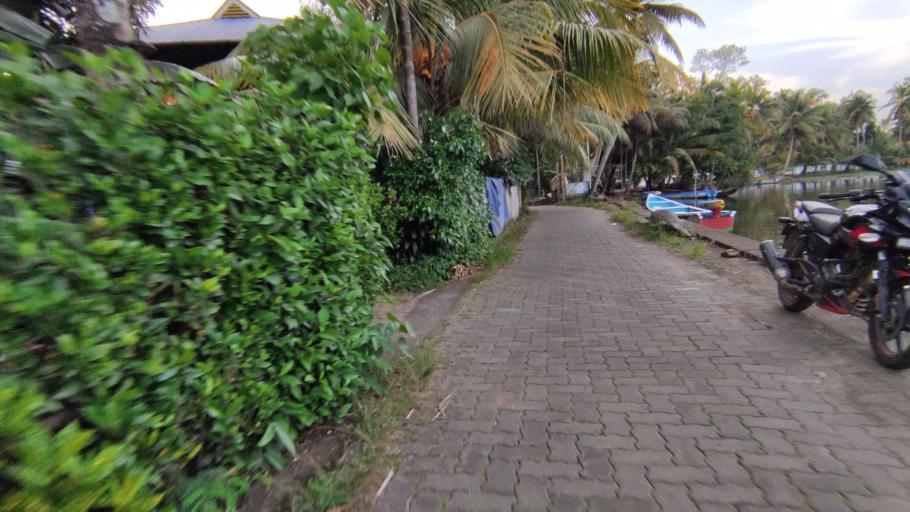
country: IN
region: Kerala
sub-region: Kottayam
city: Kottayam
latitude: 9.5789
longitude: 76.4404
